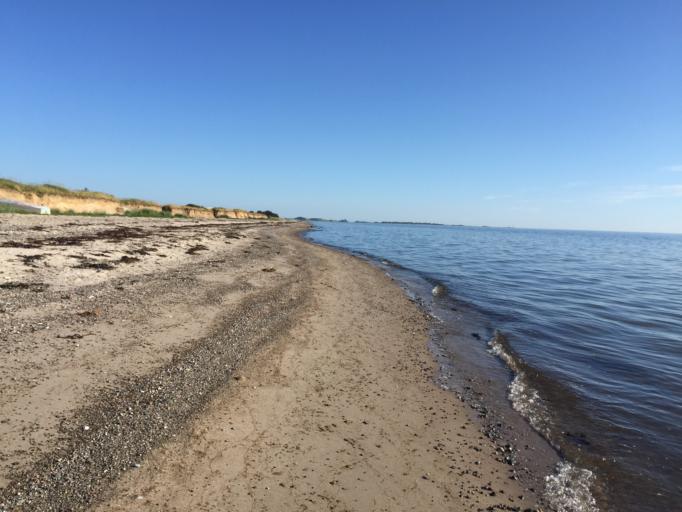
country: DK
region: Zealand
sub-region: Slagelse Kommune
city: Korsor
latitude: 55.2214
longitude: 11.1720
